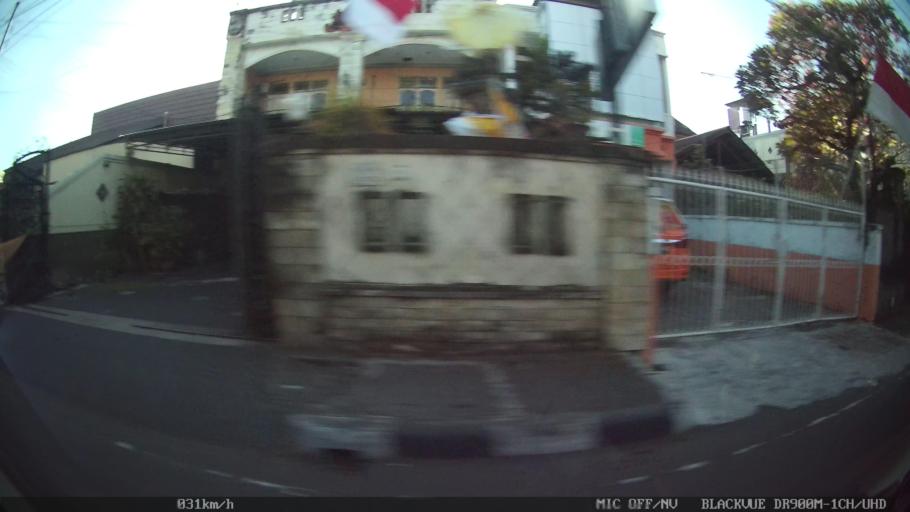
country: ID
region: Bali
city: Denpasar
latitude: -8.6410
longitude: 115.2219
